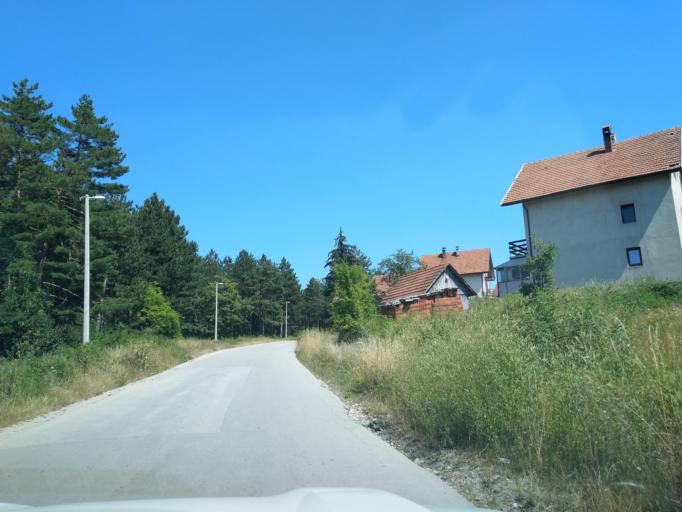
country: RS
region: Central Serbia
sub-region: Zlatiborski Okrug
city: Uzice
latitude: 43.8099
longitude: 19.8031
